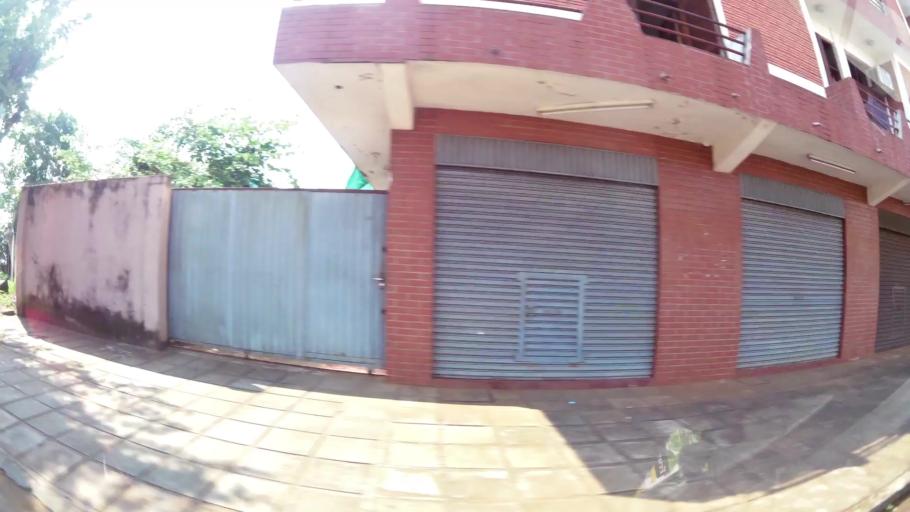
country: PY
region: Alto Parana
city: Ciudad del Este
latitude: -25.5097
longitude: -54.6251
